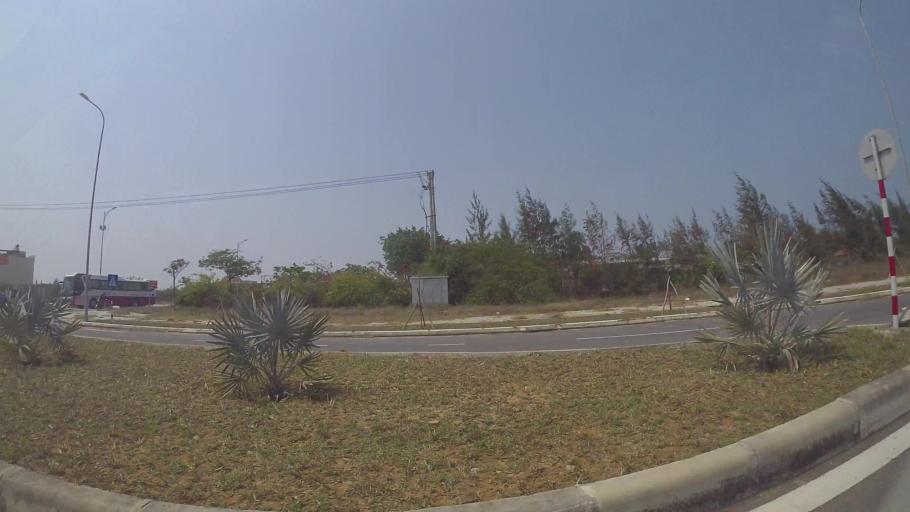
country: VN
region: Da Nang
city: Ngu Hanh Son
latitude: 15.9870
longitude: 108.2730
